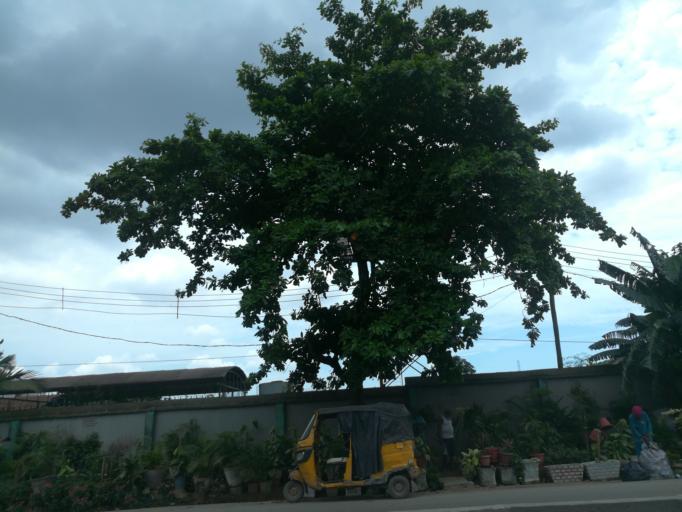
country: NG
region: Lagos
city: Ikeja
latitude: 6.5963
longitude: 3.3493
